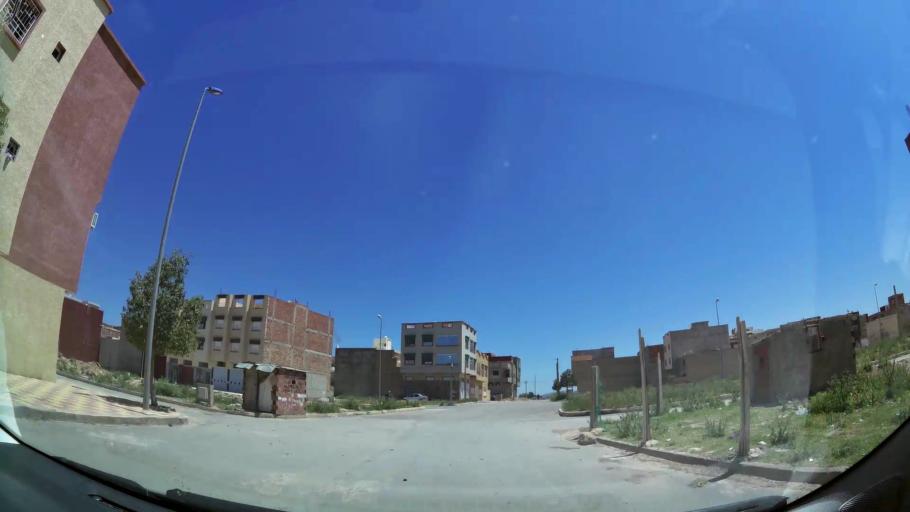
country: MA
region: Oriental
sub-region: Oujda-Angad
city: Oujda
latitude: 34.6727
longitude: -1.8776
